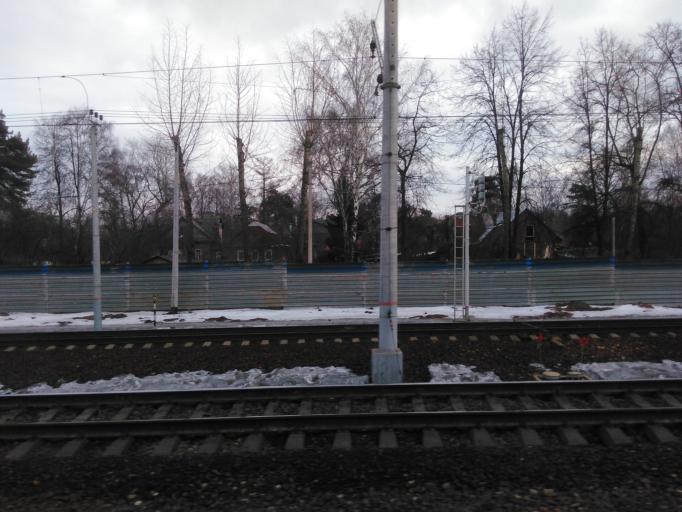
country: RU
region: Moskovskaya
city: Mytishchi
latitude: 55.9028
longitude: 37.7451
